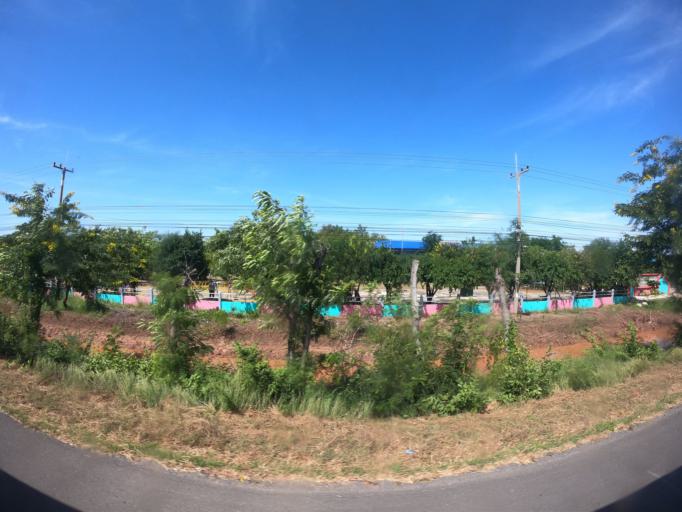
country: TH
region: Nakhon Ratchasima
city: Non Sung
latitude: 15.1955
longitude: 102.3494
